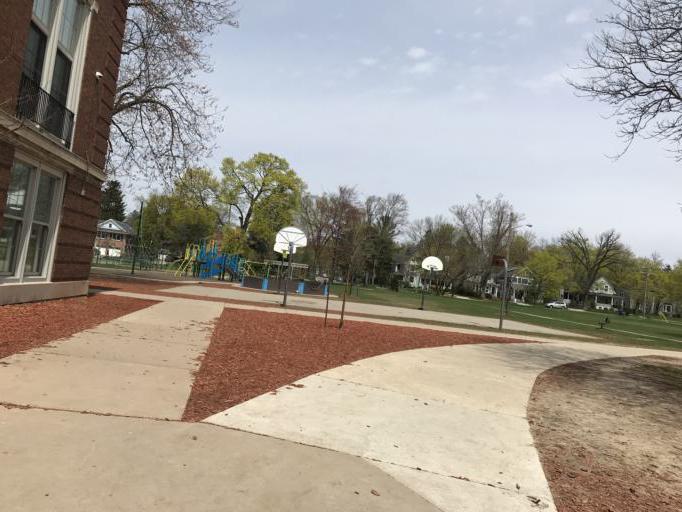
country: US
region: Michigan
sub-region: Washtenaw County
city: Ann Arbor
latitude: 42.2660
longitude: -83.7299
